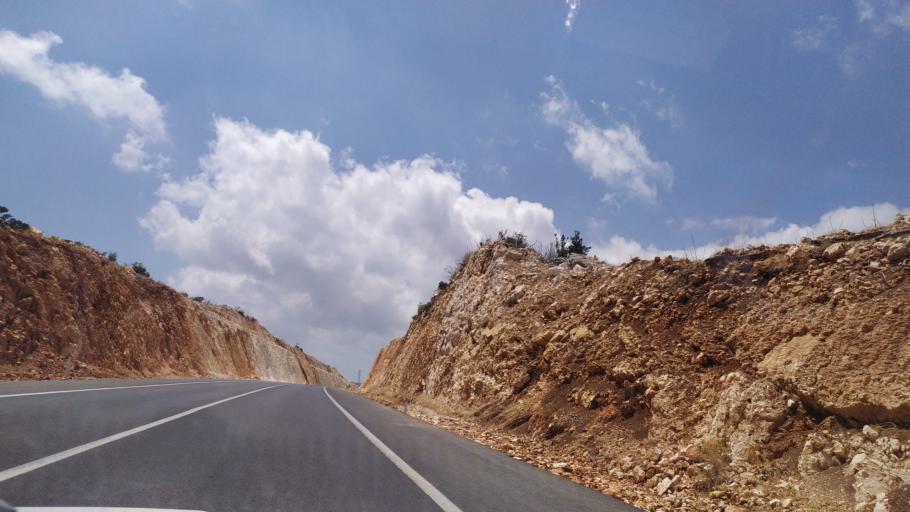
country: TR
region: Mersin
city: Gulnar
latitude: 36.2698
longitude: 33.3716
